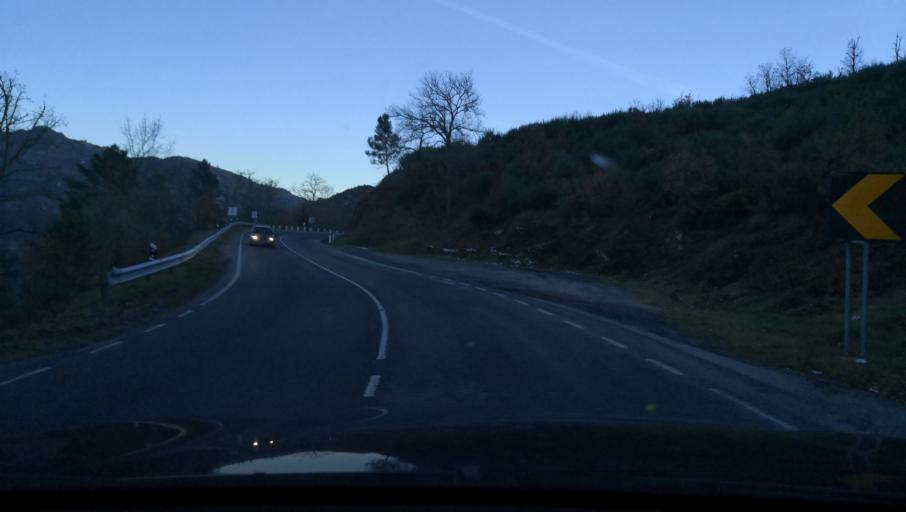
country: PT
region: Vila Real
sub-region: Vila Pouca de Aguiar
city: Vila Pouca de Aguiar
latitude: 41.4152
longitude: -7.6872
